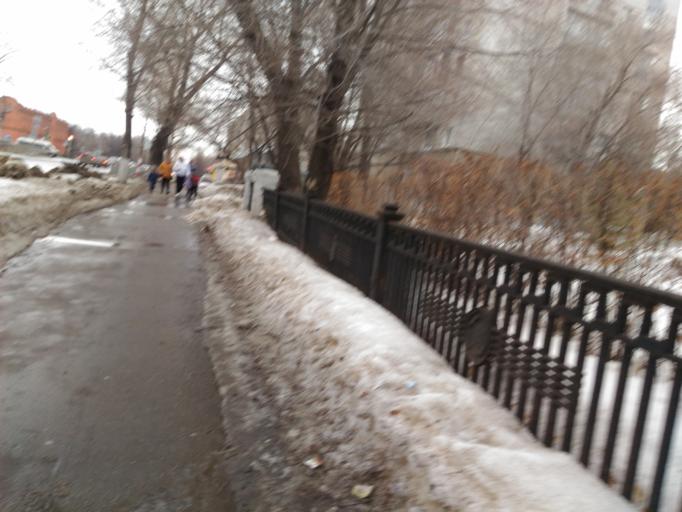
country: RU
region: Ulyanovsk
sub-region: Ulyanovskiy Rayon
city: Ulyanovsk
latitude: 54.3058
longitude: 48.3793
